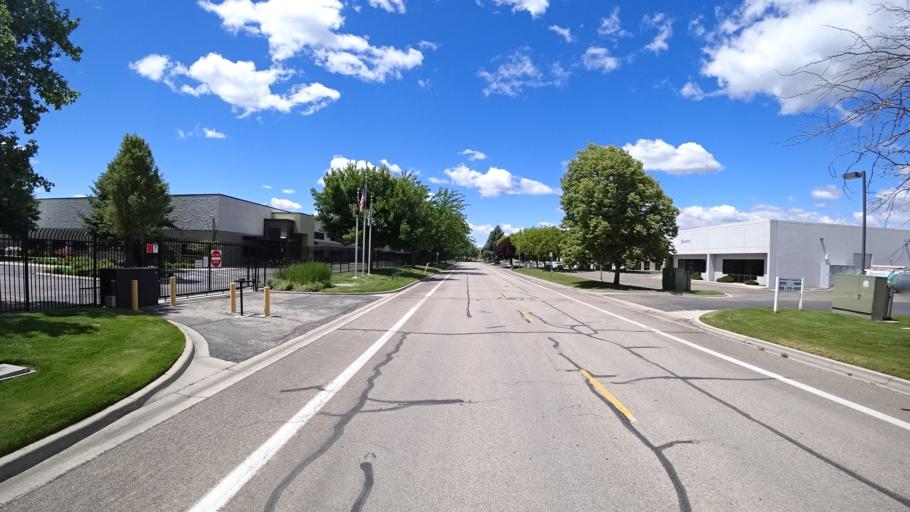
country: US
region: Idaho
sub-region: Ada County
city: Eagle
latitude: 43.6588
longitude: -116.3383
